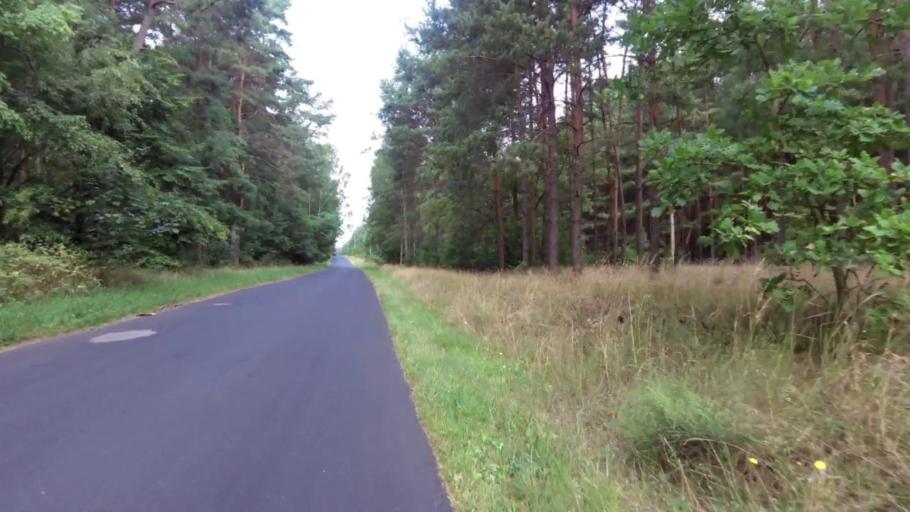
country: PL
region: West Pomeranian Voivodeship
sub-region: Powiat mysliborski
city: Debno
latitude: 52.8470
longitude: 14.7453
